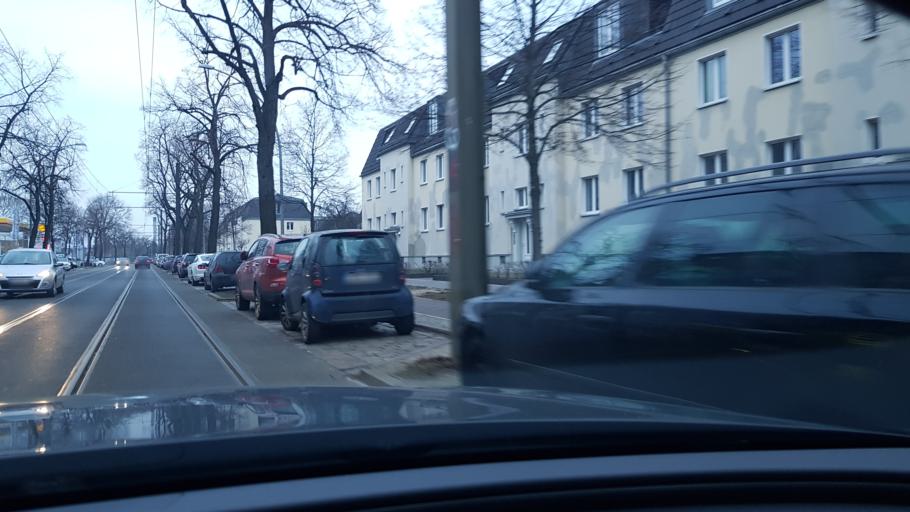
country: DE
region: Berlin
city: Grunau
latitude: 52.4282
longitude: 13.5849
